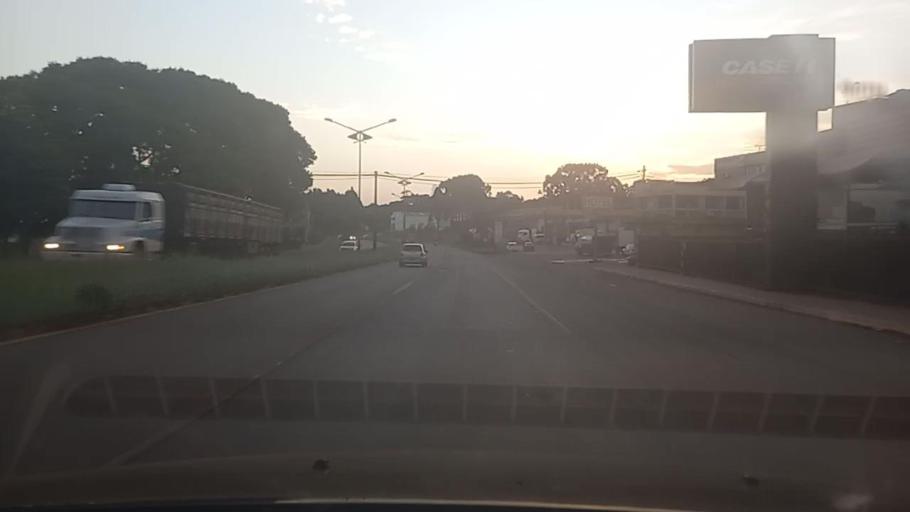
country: BR
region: Rio Grande do Sul
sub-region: Passo Fundo
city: Passo Fundo
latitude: -28.2736
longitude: -52.4452
